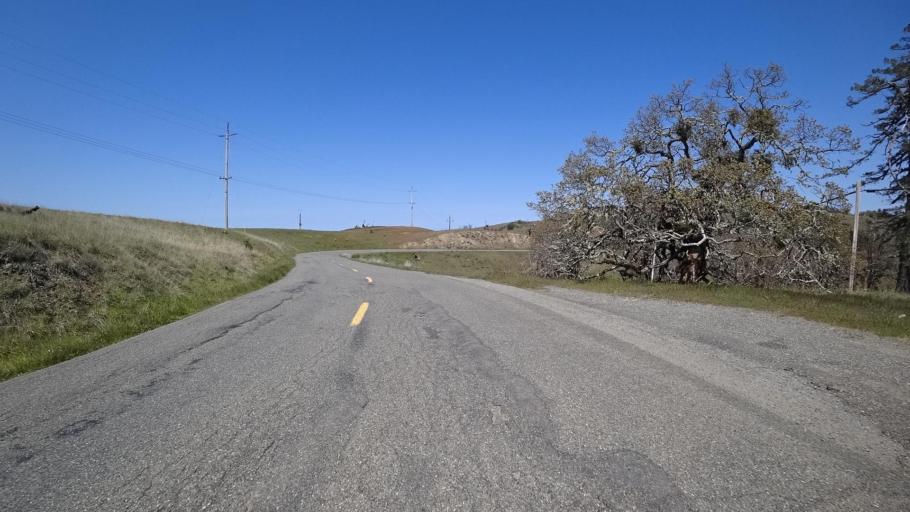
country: US
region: California
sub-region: Humboldt County
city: Redway
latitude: 40.0969
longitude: -123.6824
